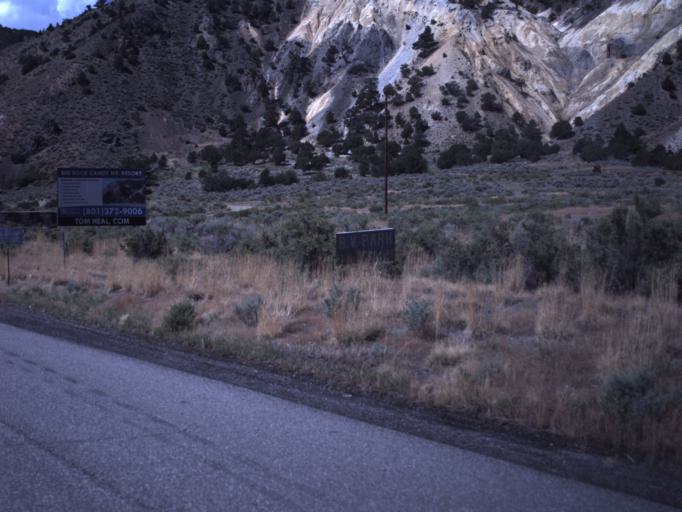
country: US
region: Utah
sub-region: Sevier County
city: Monroe
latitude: 38.5214
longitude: -112.2658
